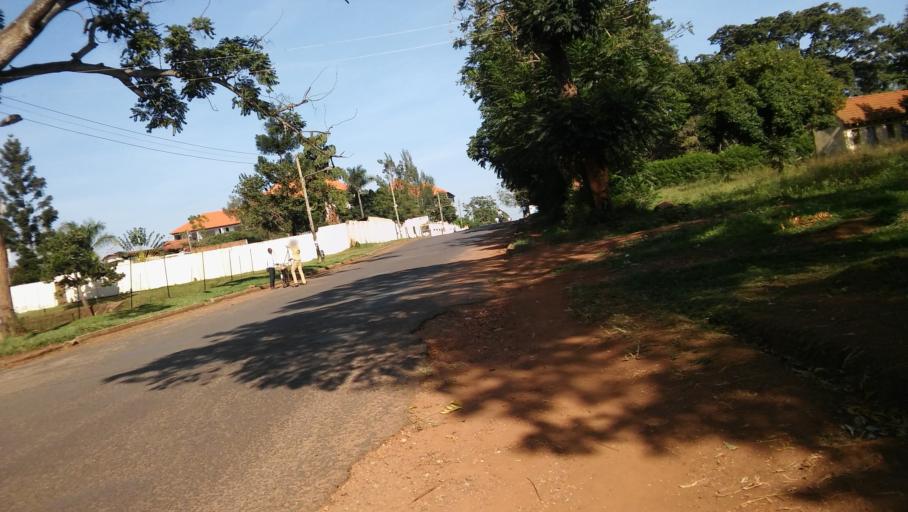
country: UG
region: Eastern Region
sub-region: Mbale District
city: Mbale
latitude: 1.0683
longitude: 34.1868
